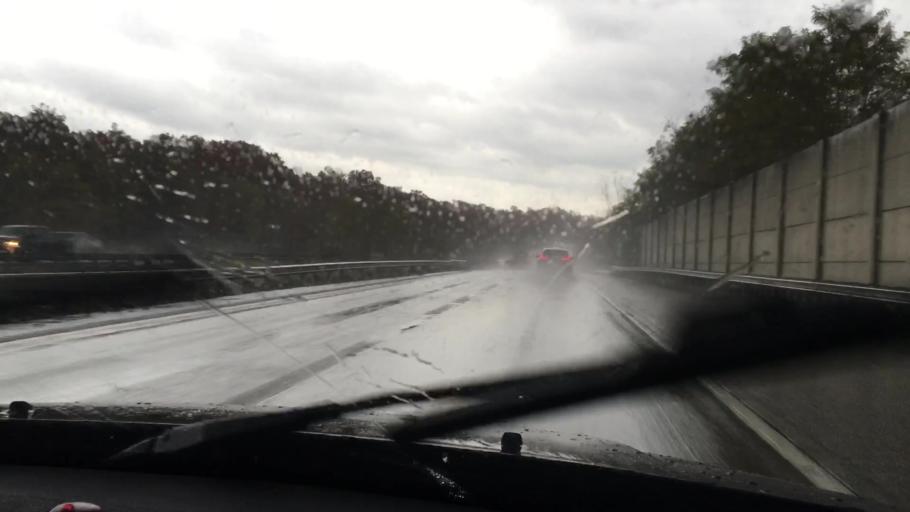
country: US
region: New Jersey
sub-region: Bergen County
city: Mahwah
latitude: 41.0929
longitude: -74.1689
